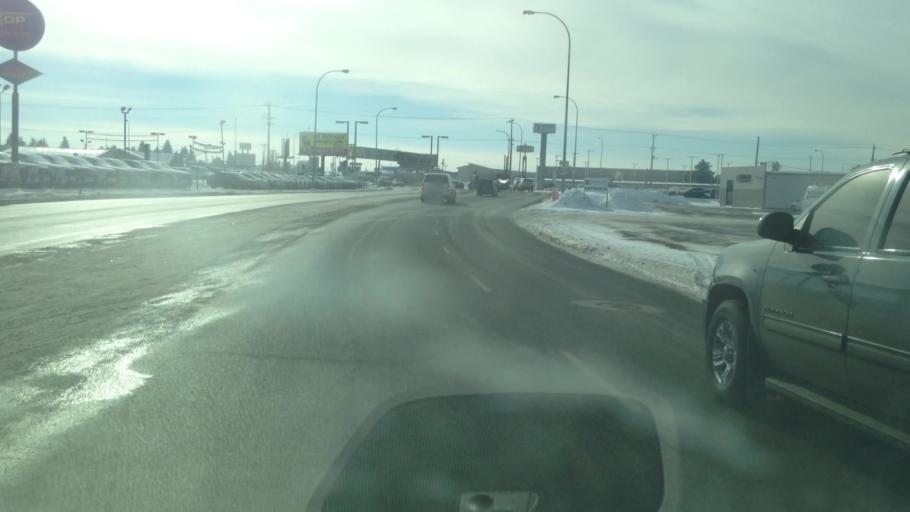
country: US
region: Idaho
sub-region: Bonneville County
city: Idaho Falls
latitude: 43.5133
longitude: -112.0237
